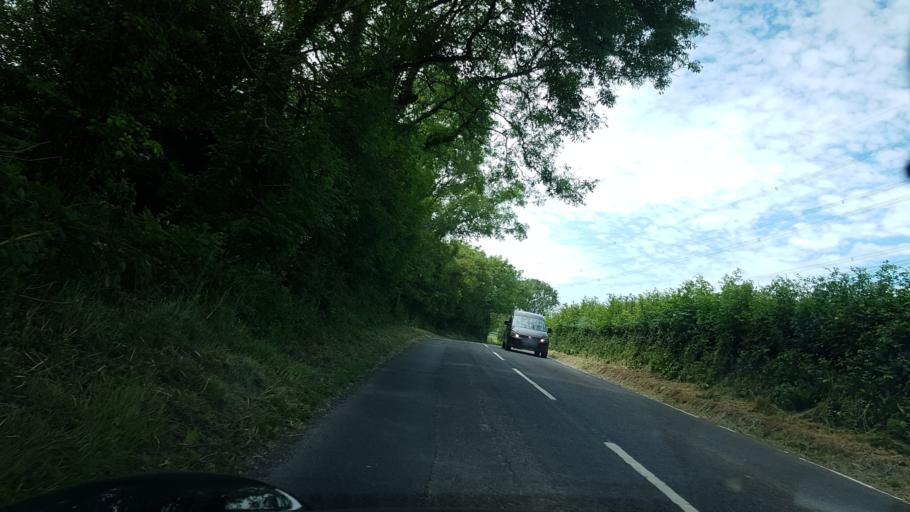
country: GB
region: Wales
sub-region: Carmarthenshire
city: Whitland
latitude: 51.7789
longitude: -4.6189
